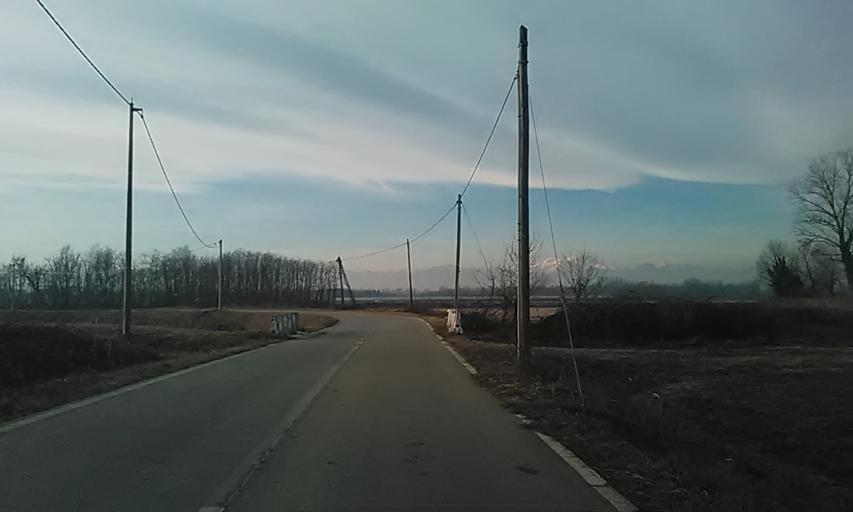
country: IT
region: Piedmont
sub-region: Provincia di Novara
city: Recetto
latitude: 45.4655
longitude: 8.4182
